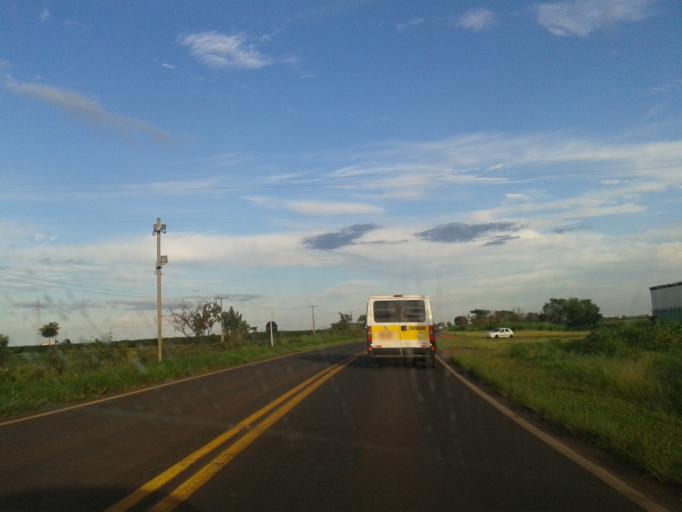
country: BR
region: Minas Gerais
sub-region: Araguari
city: Araguari
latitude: -18.6392
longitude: -48.2243
